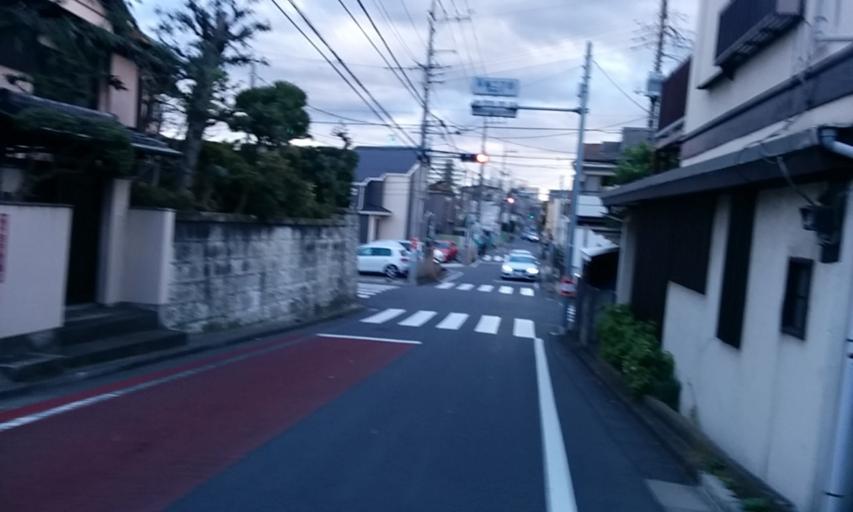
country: JP
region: Tokyo
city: Tokyo
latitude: 35.6733
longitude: 139.6370
